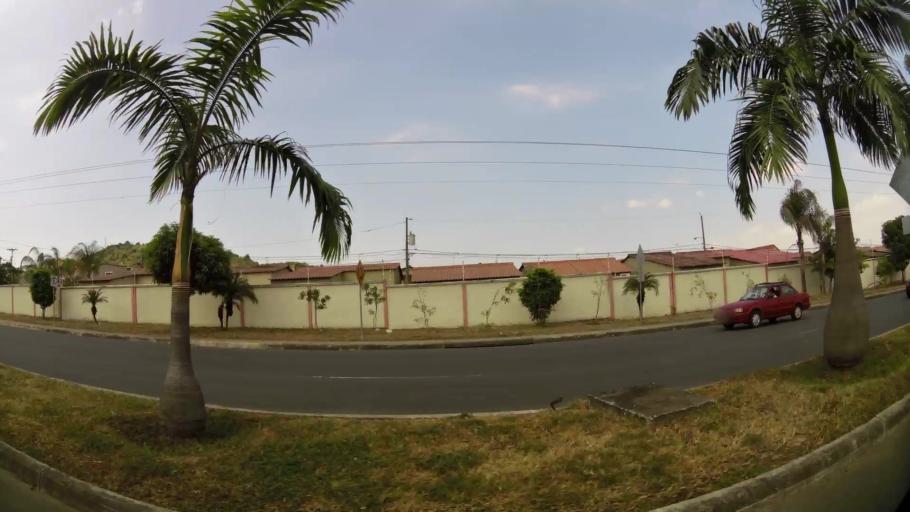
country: EC
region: Guayas
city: El Triunfo
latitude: -2.0414
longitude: -79.9149
